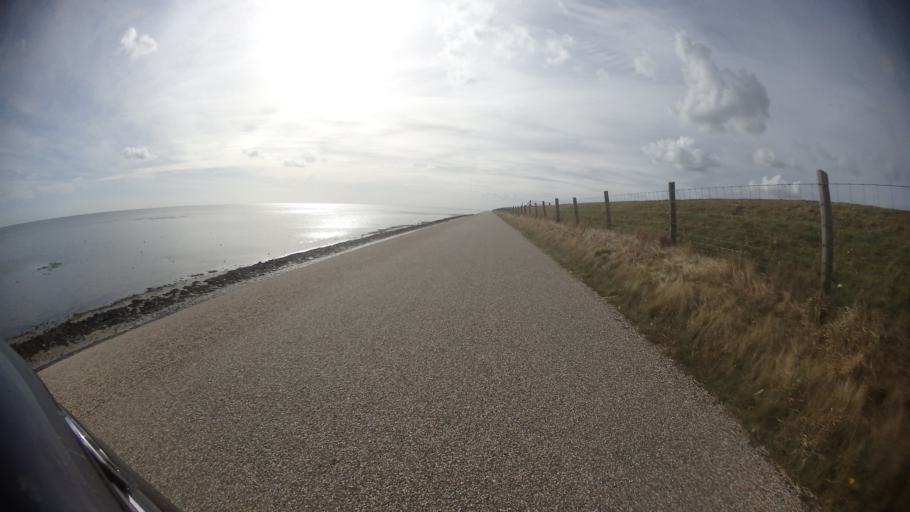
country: NL
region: North Holland
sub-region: Gemeente Texel
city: Den Burg
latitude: 53.0938
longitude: 4.8993
